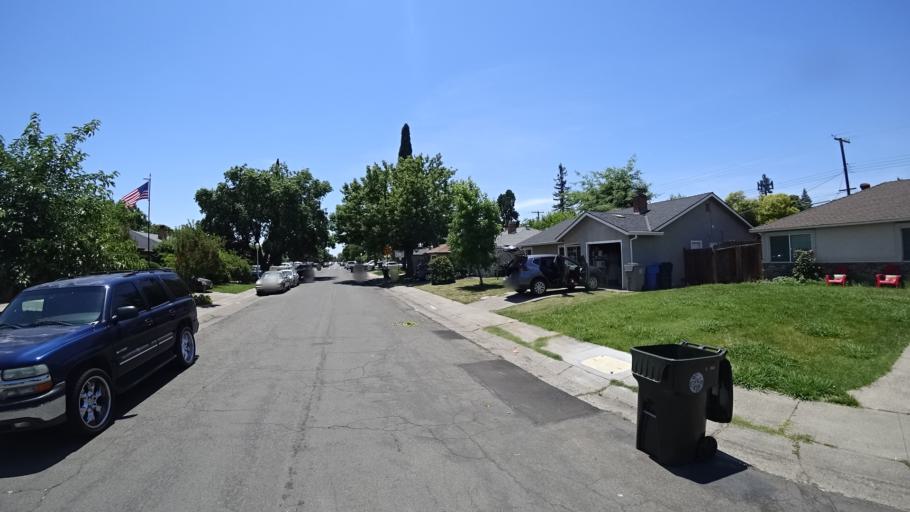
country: US
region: California
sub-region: Sacramento County
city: Florin
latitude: 38.5312
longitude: -121.4226
